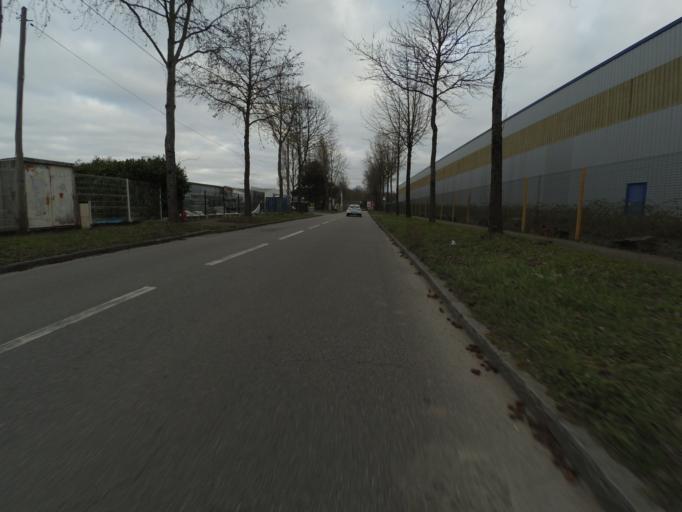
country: FR
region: Pays de la Loire
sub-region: Departement de la Loire-Atlantique
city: Sainte-Luce-sur-Loire
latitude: 47.2637
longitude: -1.4960
